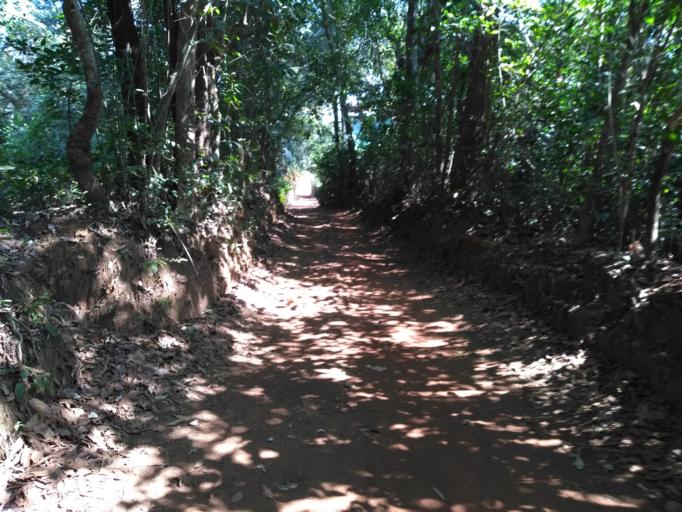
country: IN
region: Maharashtra
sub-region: Sindhudurg
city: Kudal
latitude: 16.0396
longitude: 73.6826
